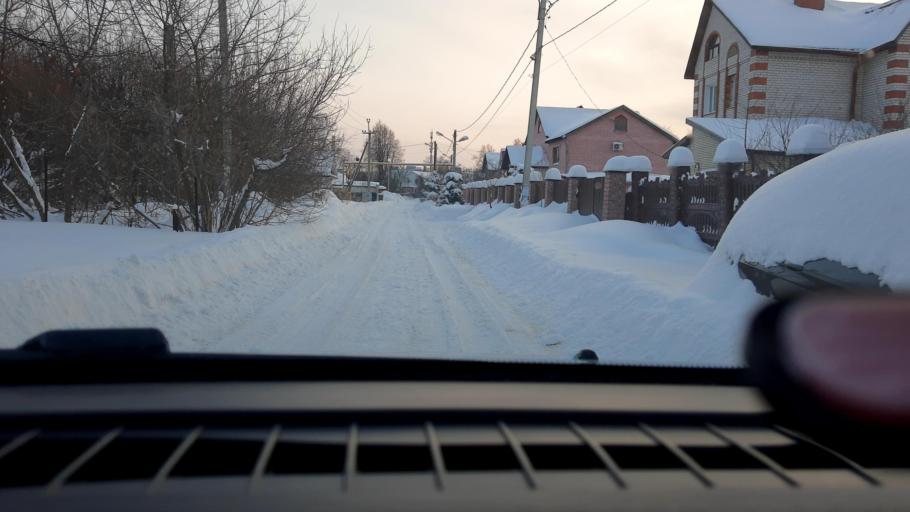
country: RU
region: Nizjnij Novgorod
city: Burevestnik
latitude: 56.2148
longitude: 43.8243
